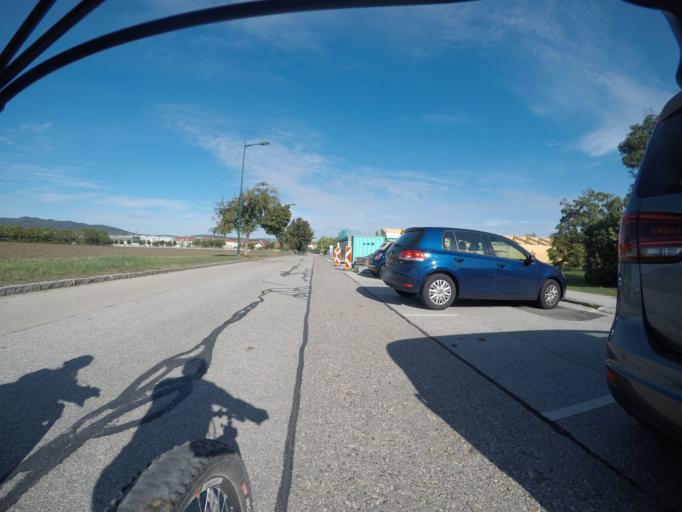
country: AT
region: Lower Austria
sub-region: Politischer Bezirk Modling
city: Modling
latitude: 48.0984
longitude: 16.3017
